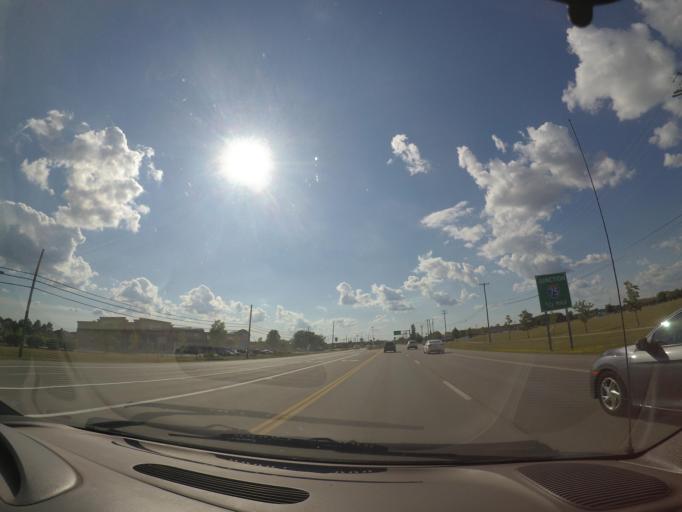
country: US
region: Ohio
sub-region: Wood County
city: Perrysburg
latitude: 41.5459
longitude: -83.5927
